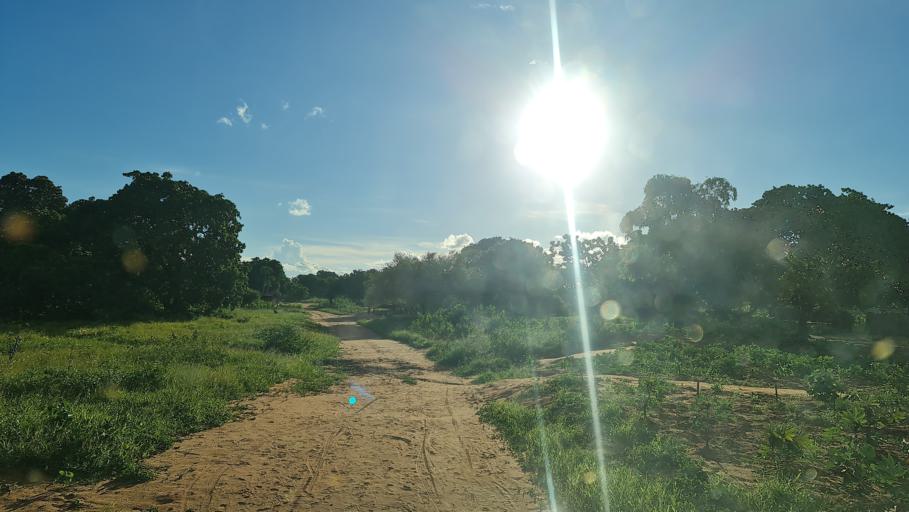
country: MZ
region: Nampula
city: Ilha de Mocambique
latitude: -14.9435
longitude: 40.1648
